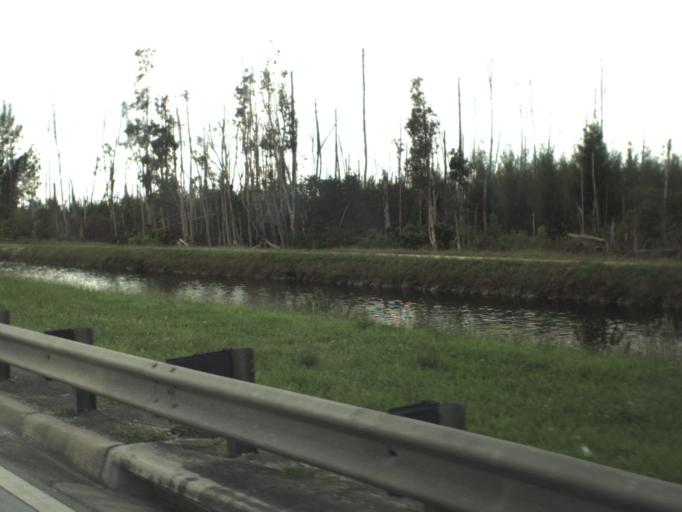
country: US
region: Florida
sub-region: Miami-Dade County
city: Tamiami
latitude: 25.7611
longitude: -80.4259
